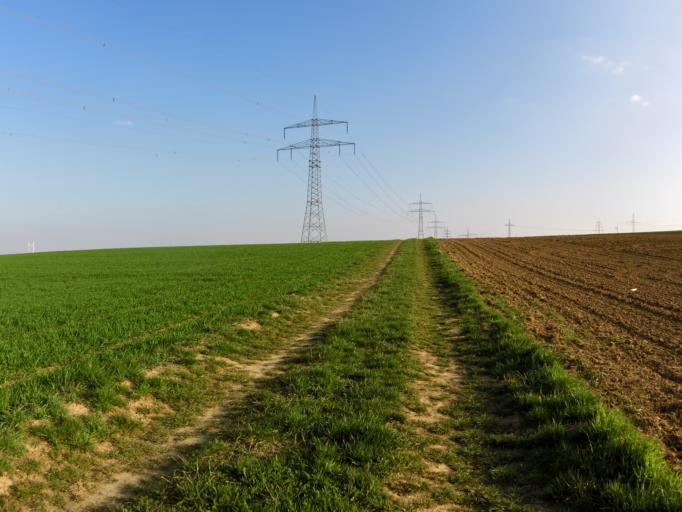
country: DE
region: Bavaria
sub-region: Regierungsbezirk Unterfranken
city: Theilheim
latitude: 49.7700
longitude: 10.0501
